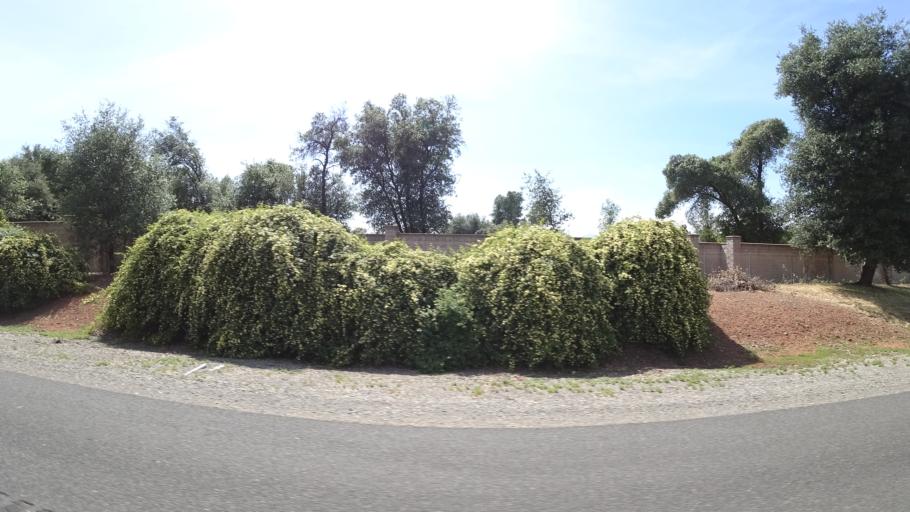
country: US
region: California
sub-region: Shasta County
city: Redding
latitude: 40.5449
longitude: -122.3533
